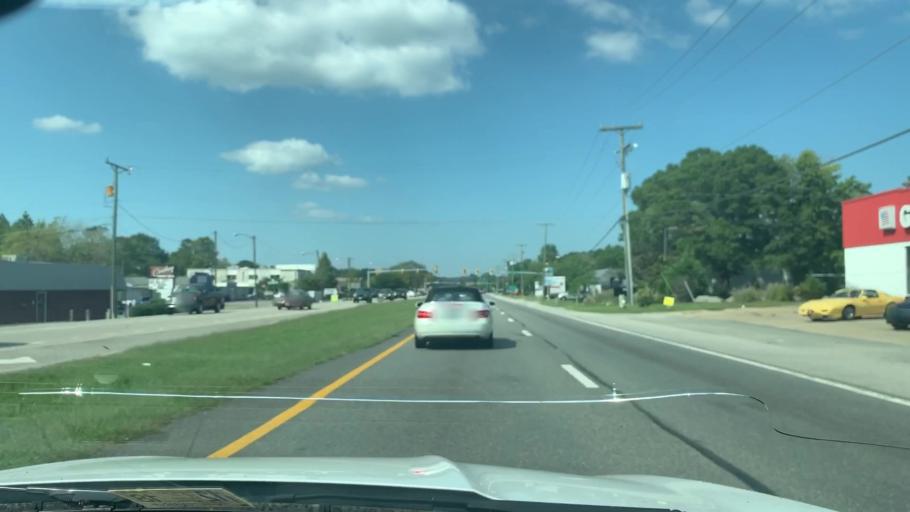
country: US
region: Virginia
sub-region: York County
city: Yorktown
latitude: 37.1696
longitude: -76.4721
